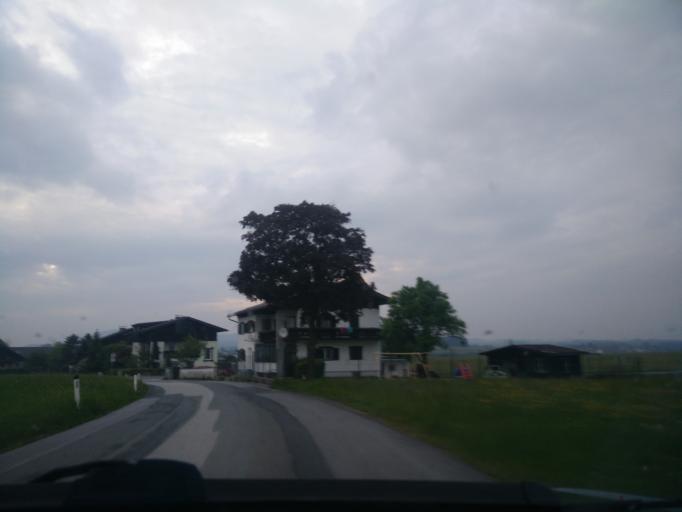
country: AT
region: Salzburg
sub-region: Politischer Bezirk Salzburg-Umgebung
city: Elixhausen
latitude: 47.8999
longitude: 13.0795
